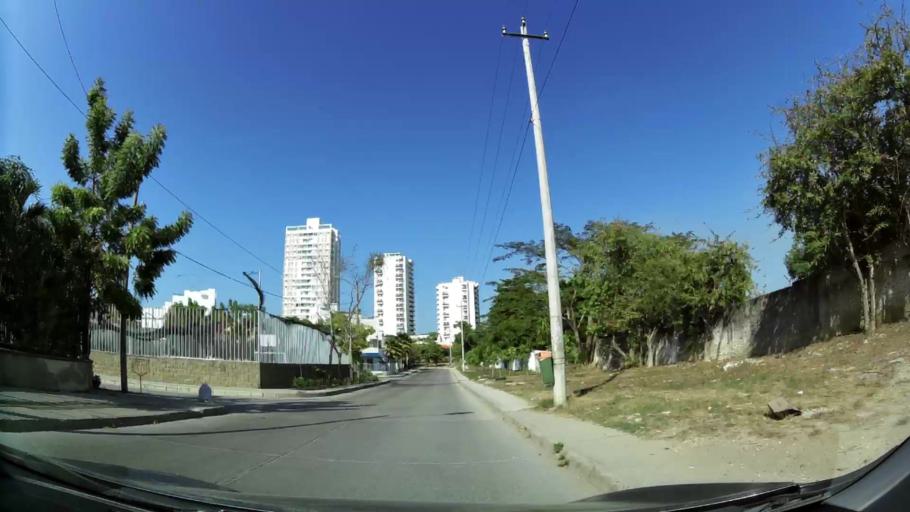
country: CO
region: Bolivar
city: Cartagena
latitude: 10.3868
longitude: -75.4759
